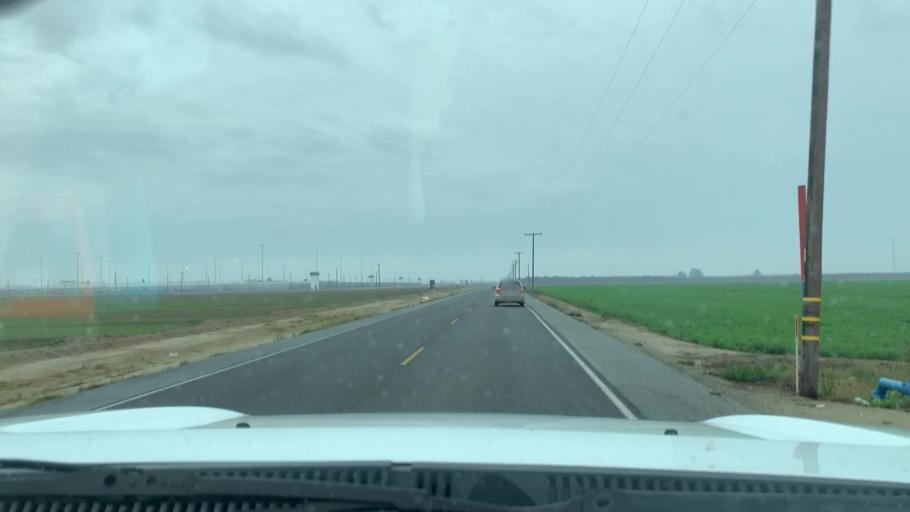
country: US
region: California
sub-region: Kern County
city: Delano
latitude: 35.7612
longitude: -119.3338
